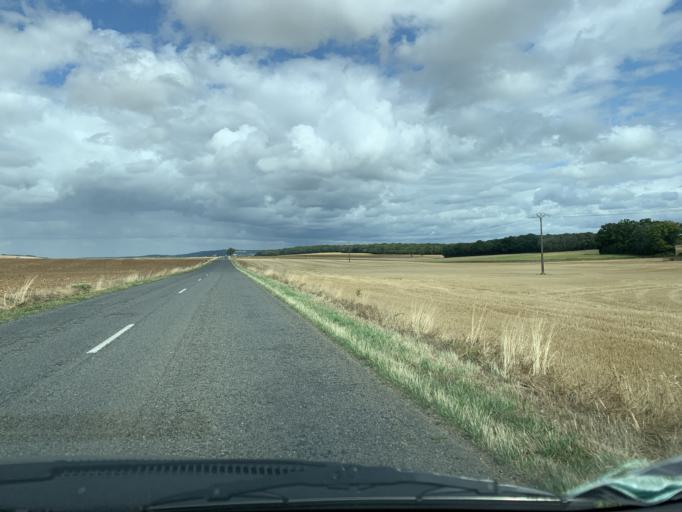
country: FR
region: Bourgogne
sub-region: Departement de la Nievre
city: Clamecy
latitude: 47.4174
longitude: 3.4621
